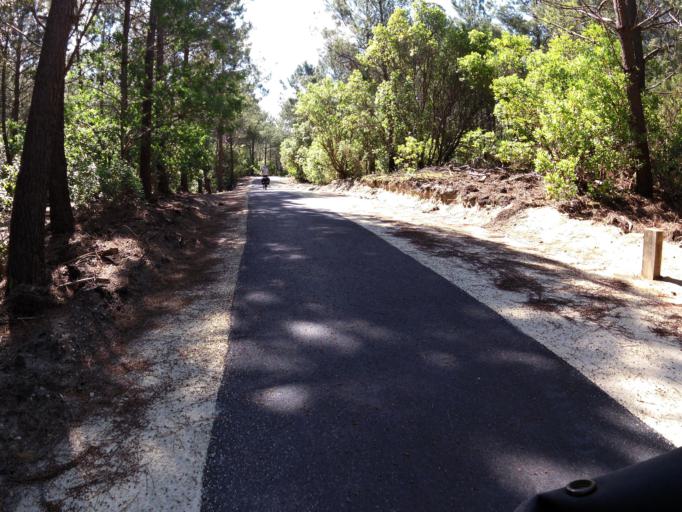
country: FR
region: Aquitaine
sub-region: Departement de la Gironde
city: Lacanau
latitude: 45.0313
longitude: -1.1615
